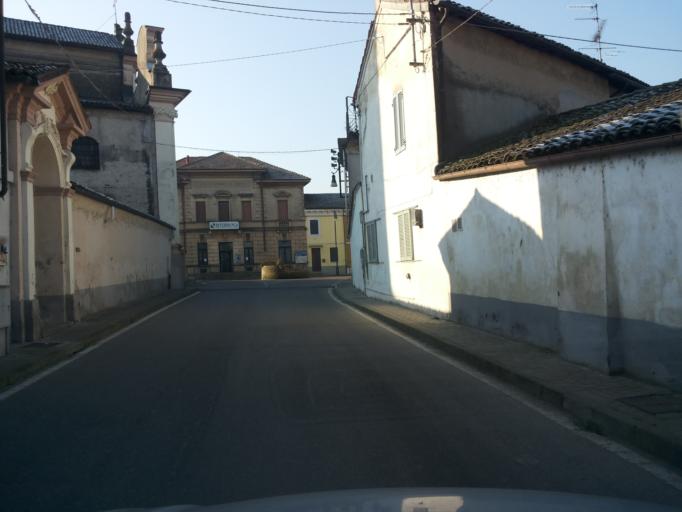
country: IT
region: Piedmont
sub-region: Provincia di Vercelli
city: Stroppiana
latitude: 45.2314
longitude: 8.4567
